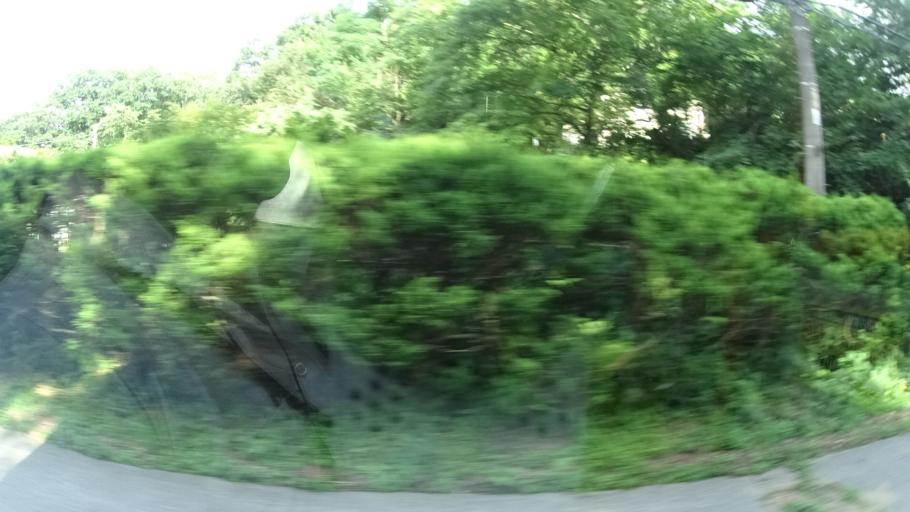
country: JP
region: Tochigi
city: Nikko
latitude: 36.6569
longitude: 139.4562
